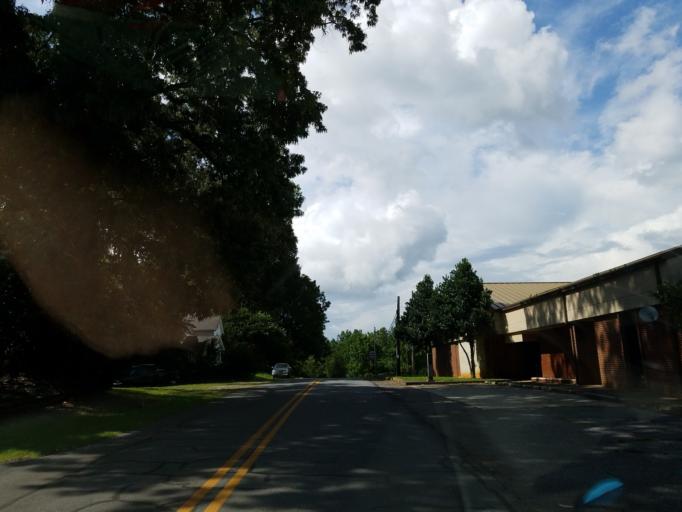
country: US
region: Georgia
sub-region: Pickens County
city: Nelson
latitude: 34.3830
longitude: -84.3729
